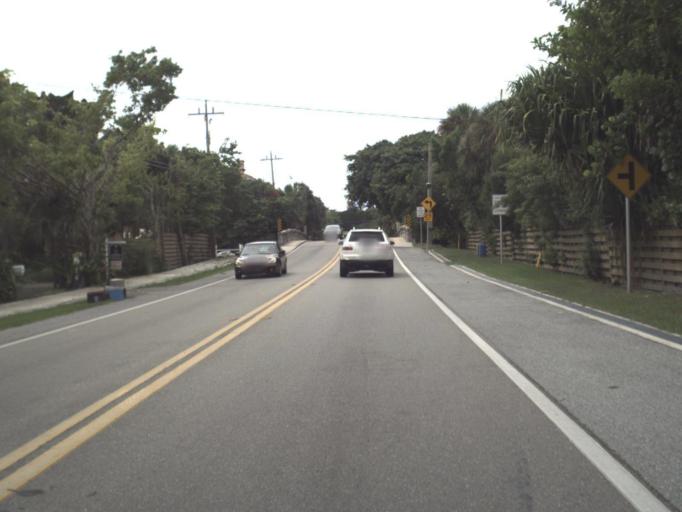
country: US
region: Florida
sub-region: Sarasota County
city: Siesta Key
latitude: 27.3020
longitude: -82.5541
